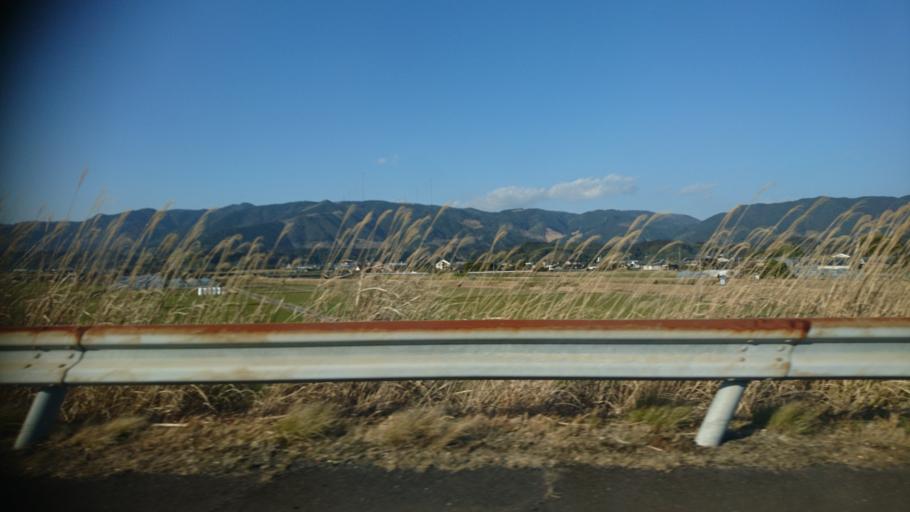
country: JP
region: Miyazaki
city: Kobayashi
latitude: 32.0366
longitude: 130.8276
